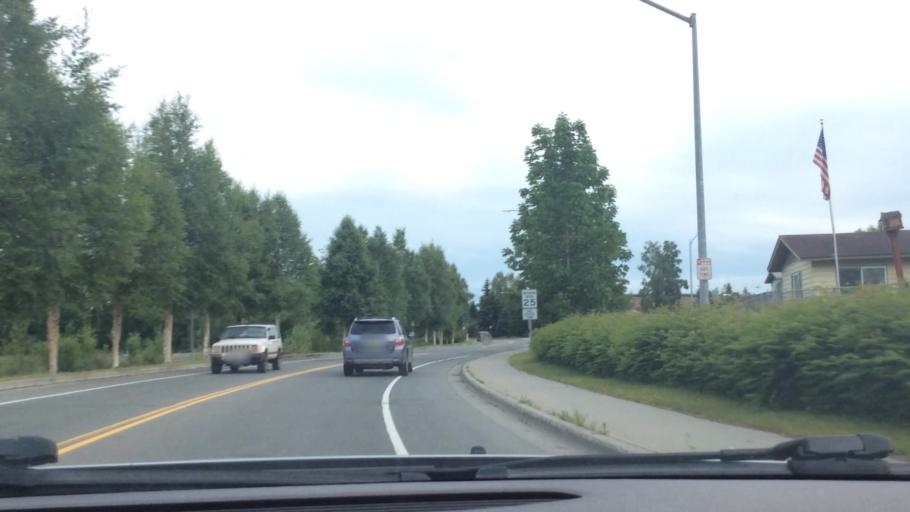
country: US
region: Alaska
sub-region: Anchorage Municipality
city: Anchorage
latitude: 61.2021
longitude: -149.7625
